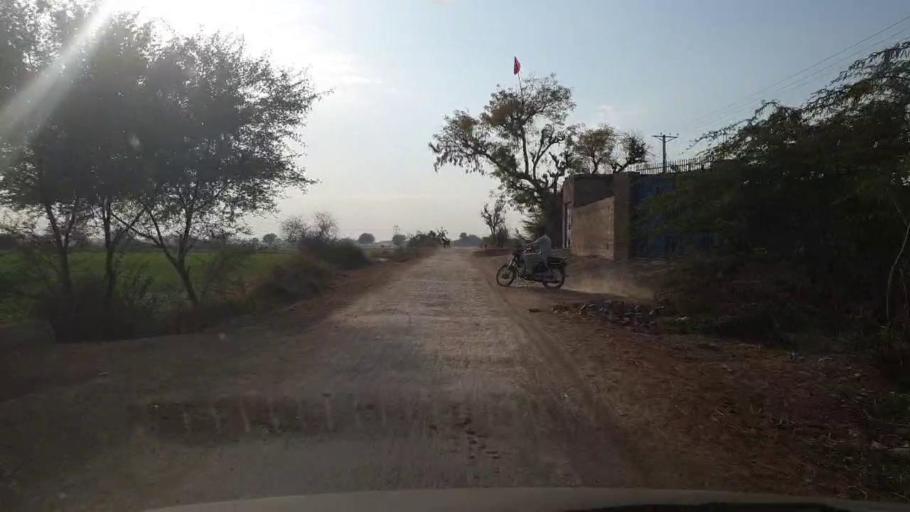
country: PK
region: Sindh
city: Sakrand
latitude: 26.0265
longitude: 68.3866
